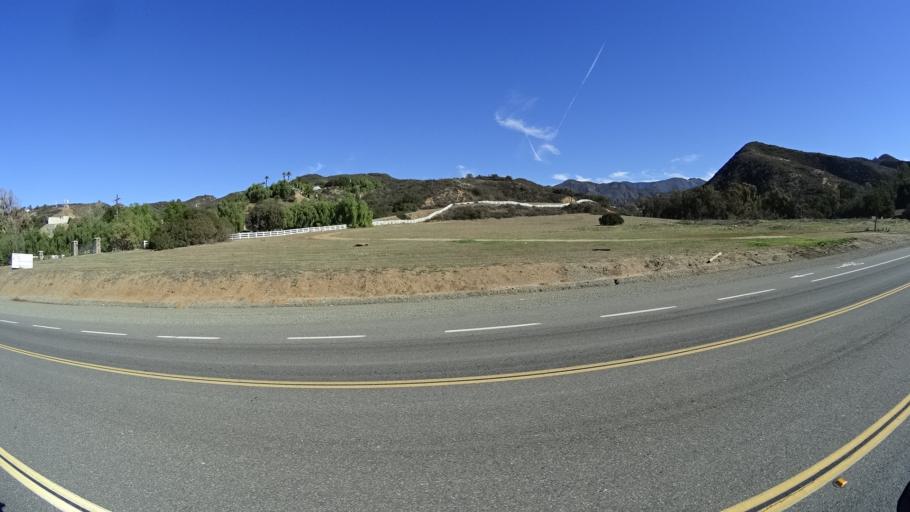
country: US
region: California
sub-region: Orange County
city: Foothill Ranch
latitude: 33.7301
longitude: -117.6509
